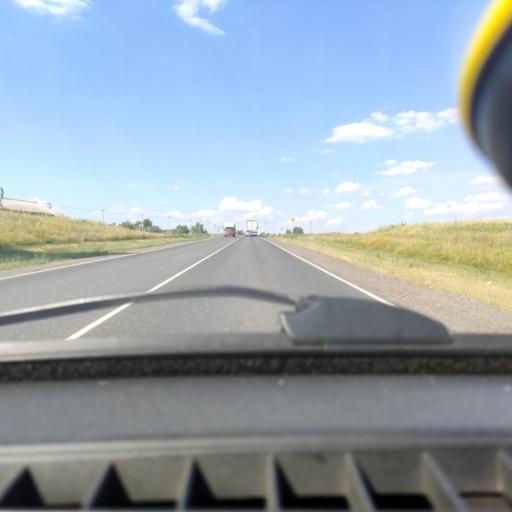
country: RU
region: Samara
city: Povolzhskiy
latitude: 53.7135
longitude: 49.7478
